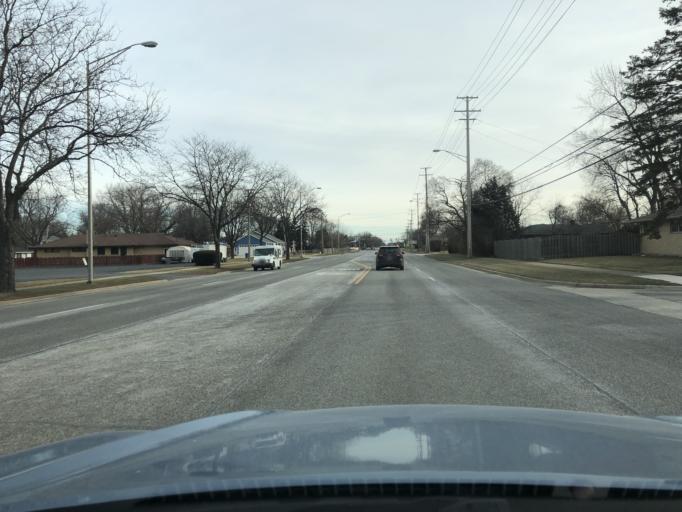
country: US
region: Illinois
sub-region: Cook County
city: Mount Prospect
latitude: 42.0662
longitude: -87.9122
